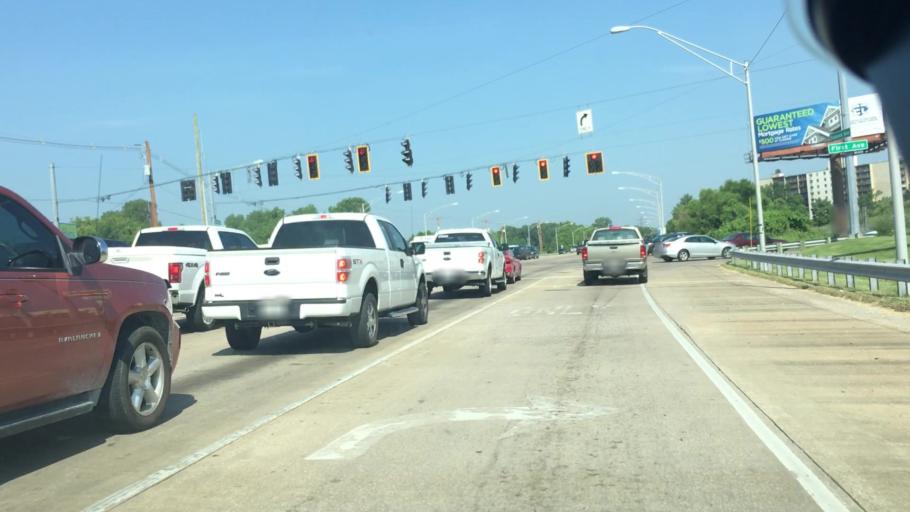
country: US
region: Indiana
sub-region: Vanderburgh County
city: Evansville
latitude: 38.0006
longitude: -87.5739
